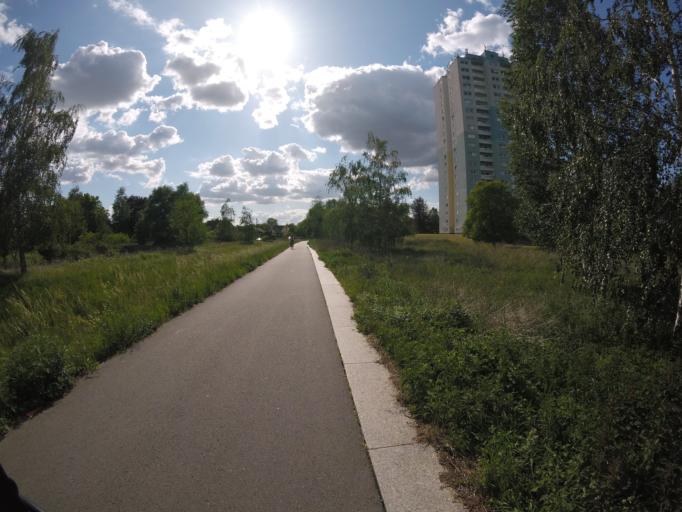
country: DE
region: Berlin
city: Wilhelmstadt
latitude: 52.5308
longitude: 13.1658
